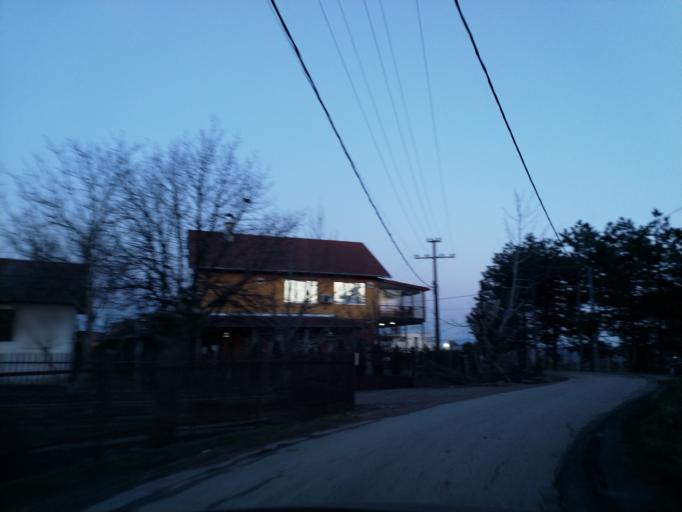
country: RS
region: Central Serbia
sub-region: Pomoravski Okrug
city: Paracin
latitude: 43.8724
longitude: 21.4188
